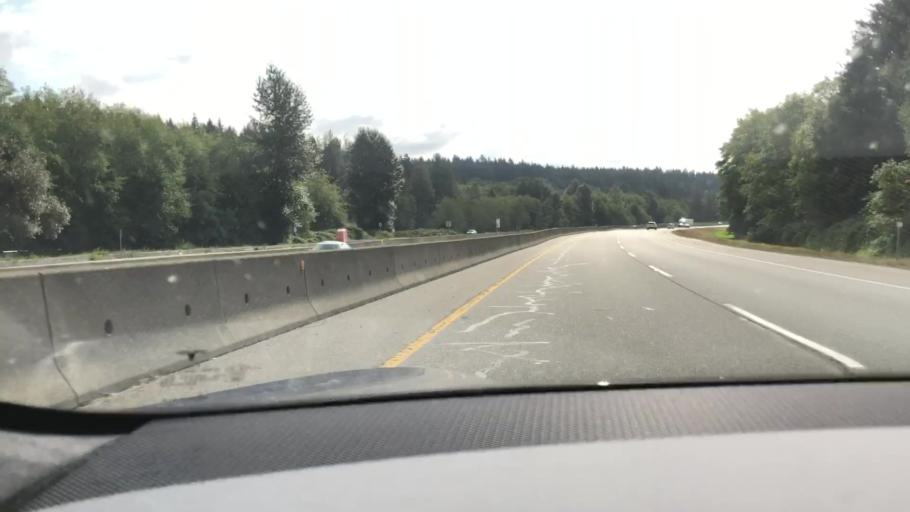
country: CA
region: British Columbia
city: Delta
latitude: 49.1135
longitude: -122.9118
